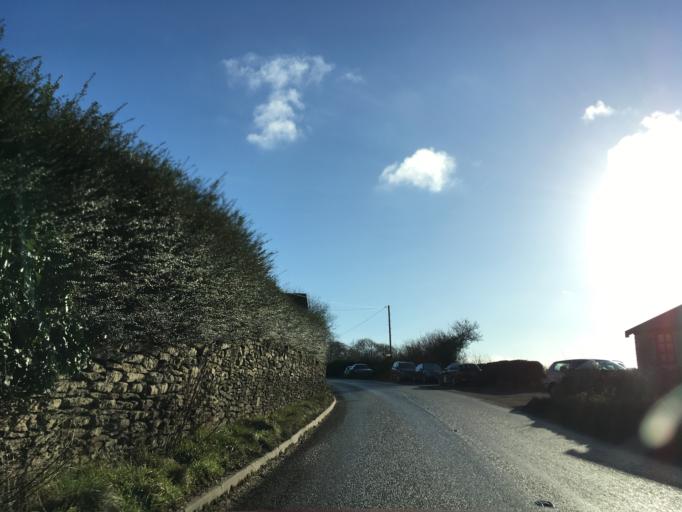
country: GB
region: England
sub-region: Wiltshire
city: Nettleton
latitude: 51.5131
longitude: -2.2413
